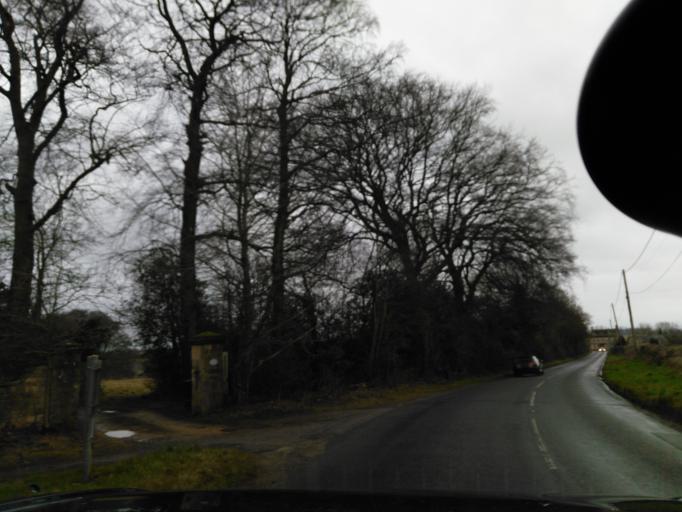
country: GB
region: England
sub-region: Wiltshire
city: Box
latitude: 51.4046
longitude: -2.2433
